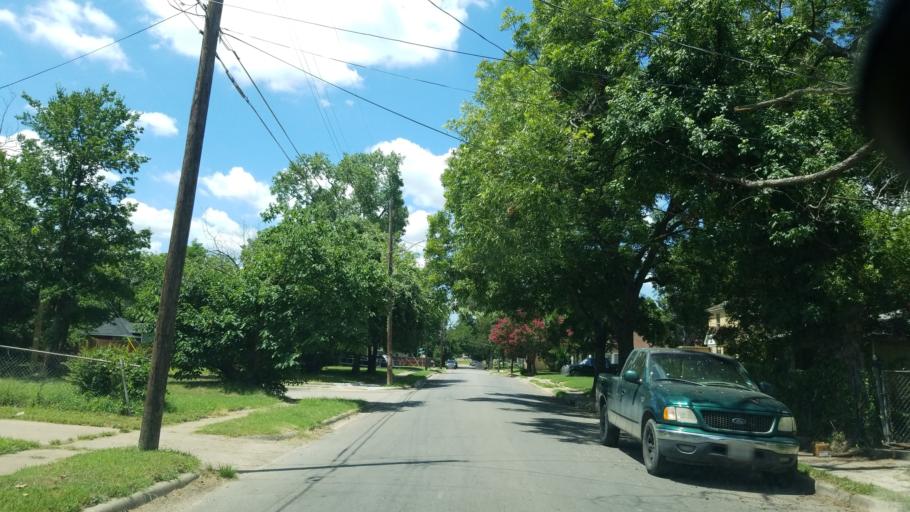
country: US
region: Texas
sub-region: Dallas County
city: Dallas
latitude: 32.7509
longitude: -96.7578
